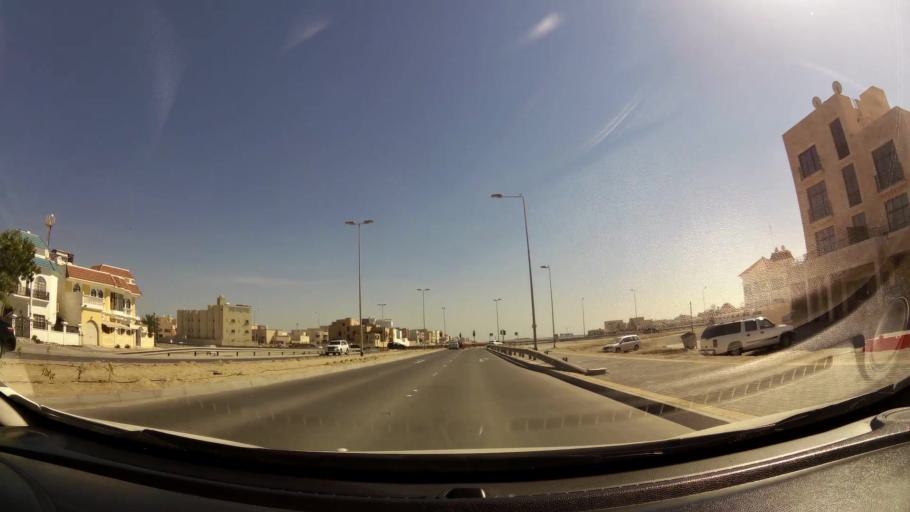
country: BH
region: Muharraq
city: Al Hadd
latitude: 26.2480
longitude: 50.6404
